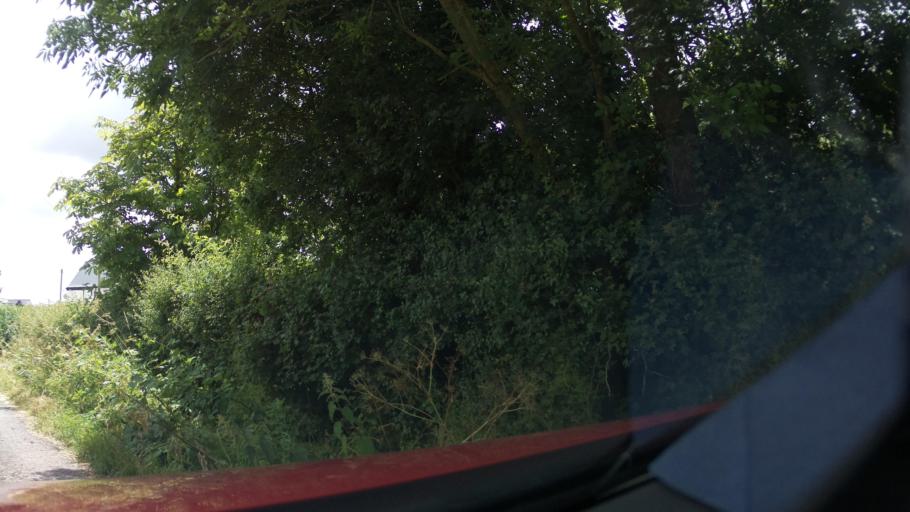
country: GB
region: England
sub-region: Wiltshire
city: Lyneham
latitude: 51.5612
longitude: -1.9791
